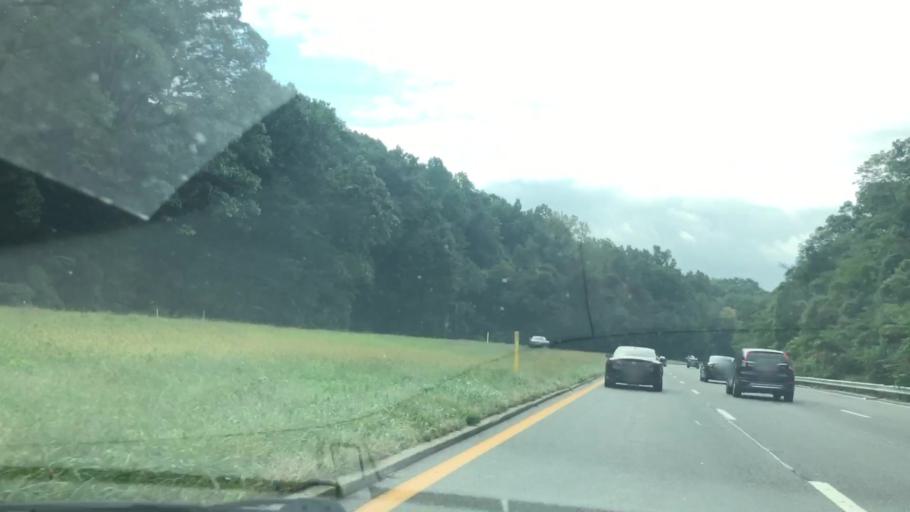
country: US
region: New York
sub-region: Westchester County
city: Yonkers
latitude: 40.9414
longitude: -73.8757
